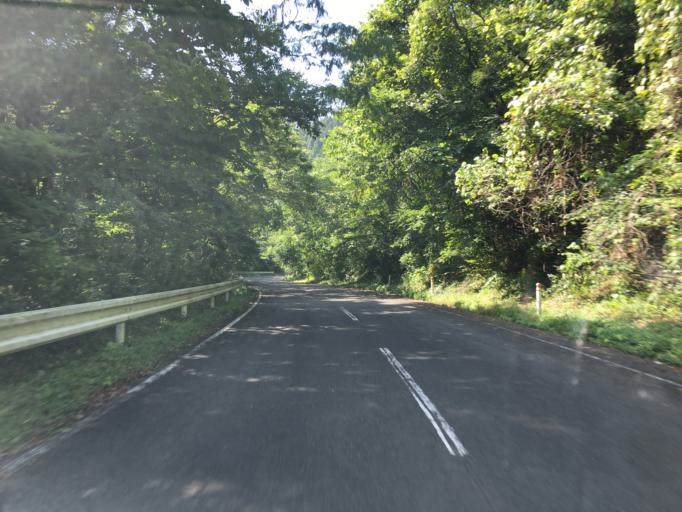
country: JP
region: Miyagi
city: Marumori
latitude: 37.8859
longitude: 140.8473
